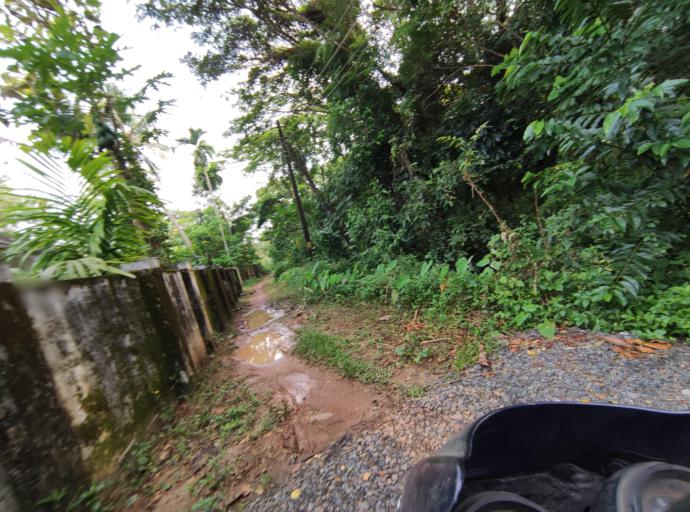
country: IN
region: Kerala
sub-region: Alappuzha
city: Vayalar
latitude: 9.6940
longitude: 76.3413
